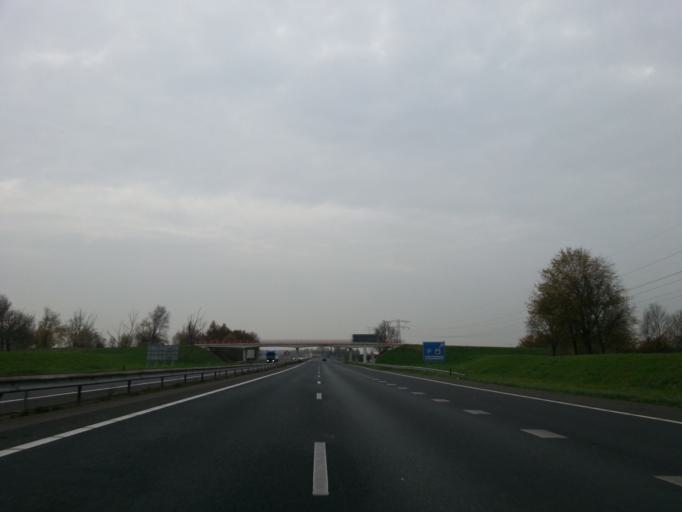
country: NL
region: North Brabant
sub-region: Gemeente Moerdijk
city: Willemstad
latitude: 51.7447
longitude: 4.4133
